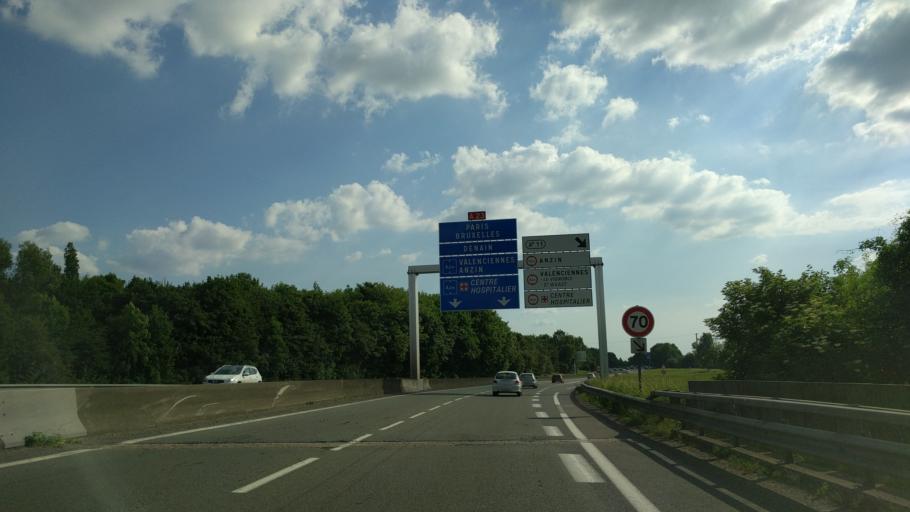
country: FR
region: Nord-Pas-de-Calais
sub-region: Departement du Nord
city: La Sentinelle
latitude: 50.3570
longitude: 3.4852
